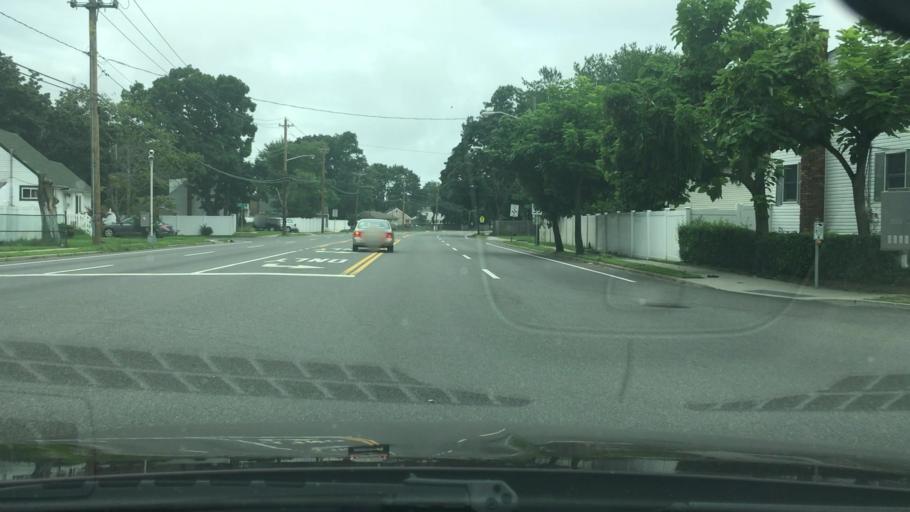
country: US
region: New York
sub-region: Suffolk County
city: Copiague
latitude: 40.6919
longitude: -73.3938
